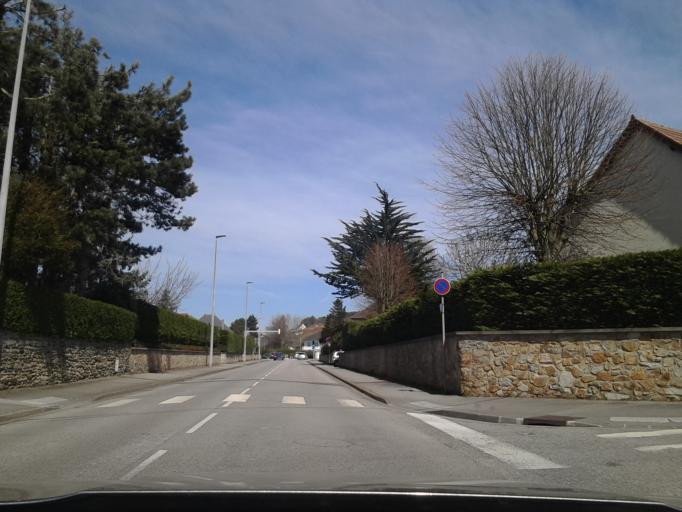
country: FR
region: Lower Normandy
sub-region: Departement de la Manche
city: Tourlaville
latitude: 49.6389
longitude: -1.5736
